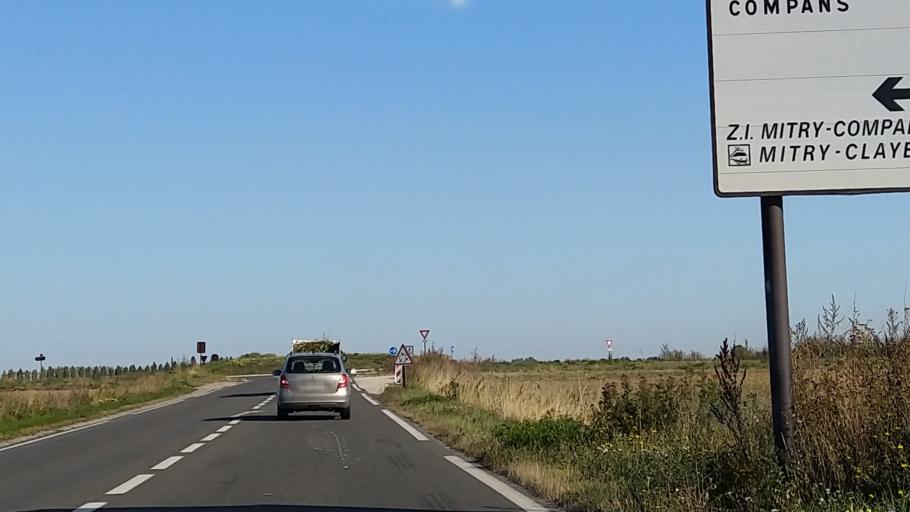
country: FR
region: Ile-de-France
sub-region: Departement de Seine-et-Marne
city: Claye-Souilly
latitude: 48.9759
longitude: 2.6607
